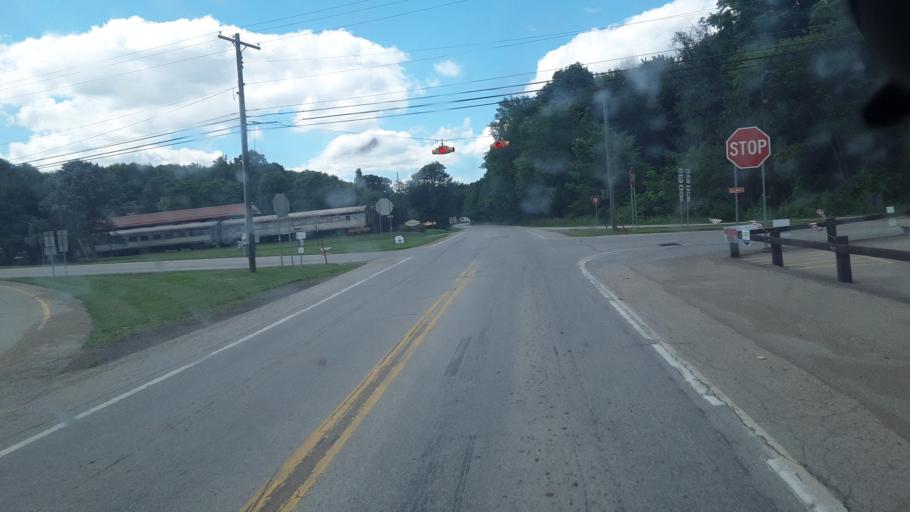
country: US
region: Pennsylvania
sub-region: Butler County
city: Slippery Rock
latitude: 41.0240
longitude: -80.1874
